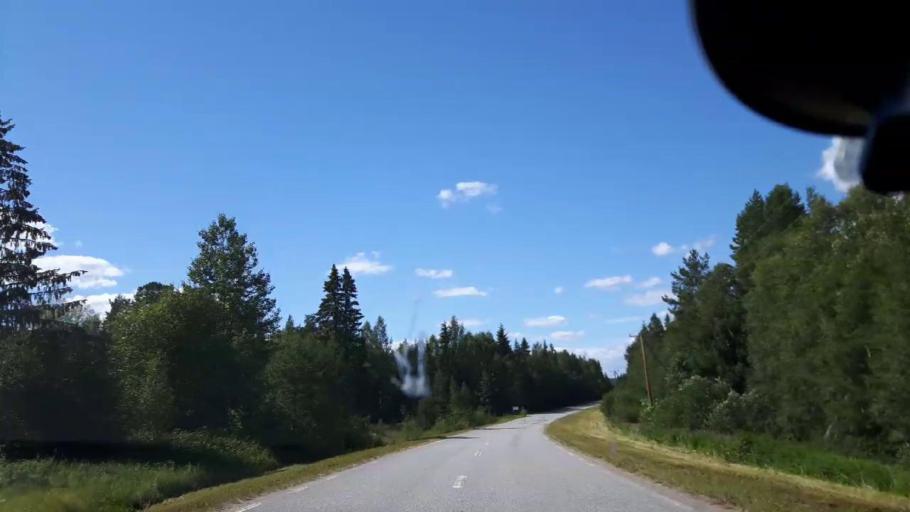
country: SE
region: Vaesternorrland
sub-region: Ange Kommun
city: Fransta
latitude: 62.7038
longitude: 16.3663
